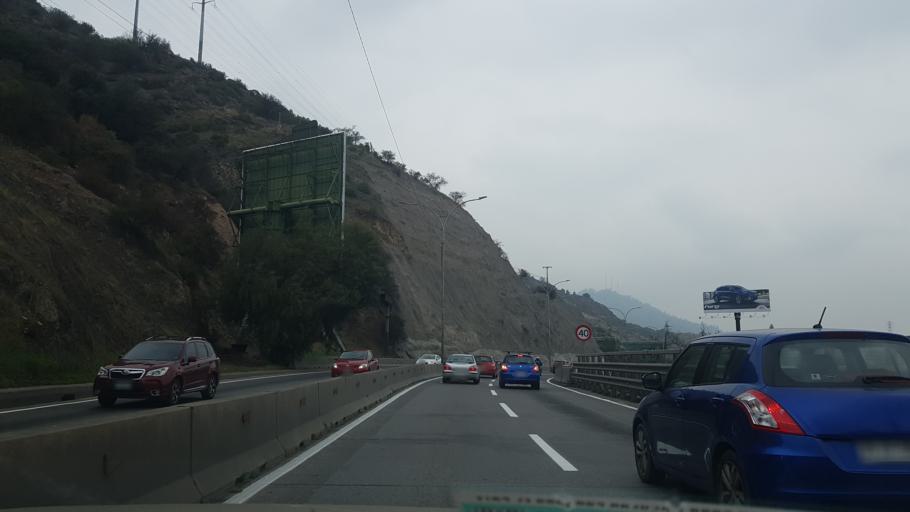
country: CL
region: Santiago Metropolitan
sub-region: Provincia de Santiago
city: Villa Presidente Frei, Nunoa, Santiago, Chile
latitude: -33.3940
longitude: -70.6091
